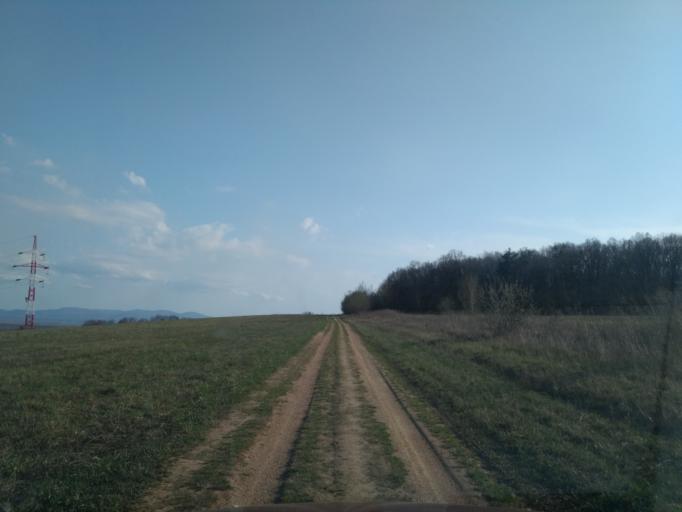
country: SK
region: Kosicky
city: Kosice
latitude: 48.6820
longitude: 21.1811
